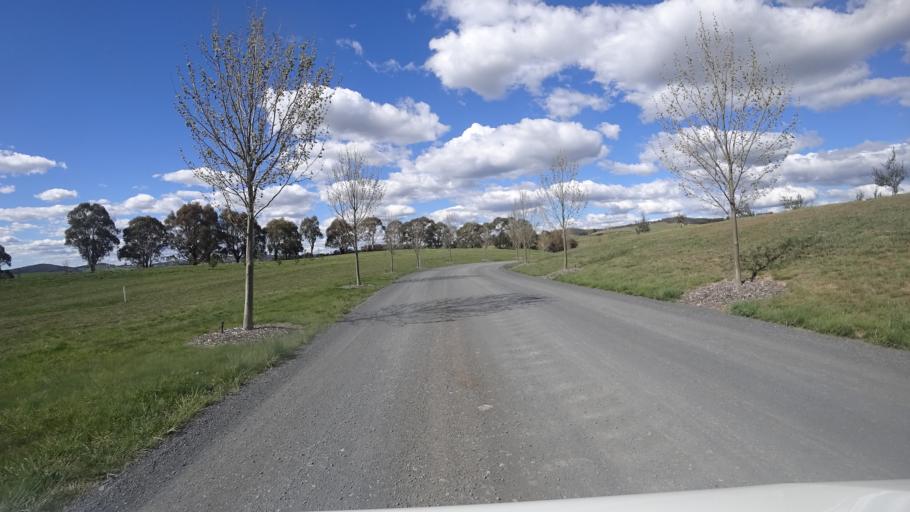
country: AU
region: New South Wales
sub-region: Oberon
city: Oberon
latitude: -33.6656
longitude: 149.7751
